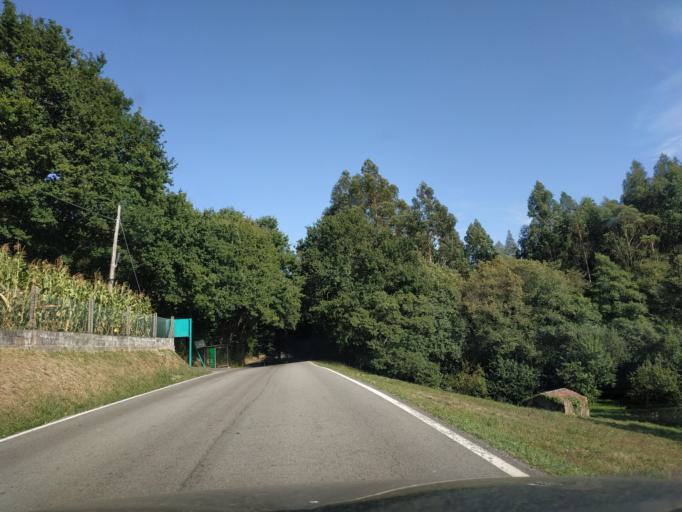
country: ES
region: Galicia
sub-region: Provincia da Coruna
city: Cerceda
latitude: 43.2339
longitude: -8.4832
